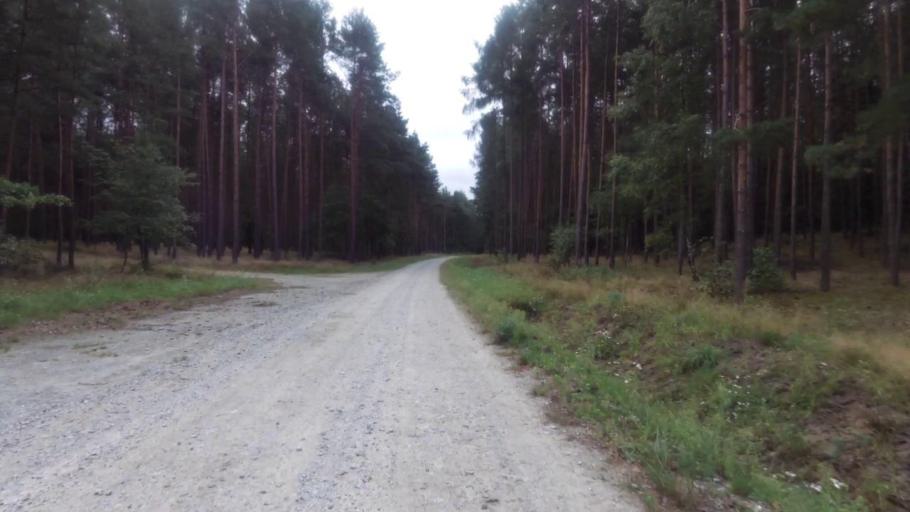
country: PL
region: West Pomeranian Voivodeship
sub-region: Powiat mysliborski
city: Boleszkowice
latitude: 52.6690
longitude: 14.6164
